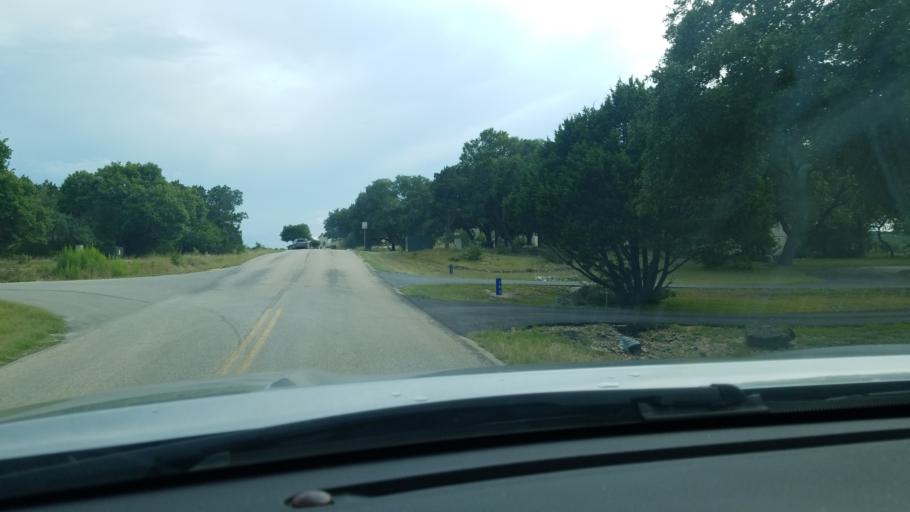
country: US
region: Texas
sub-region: Comal County
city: Bulverde
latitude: 29.8396
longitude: -98.4049
